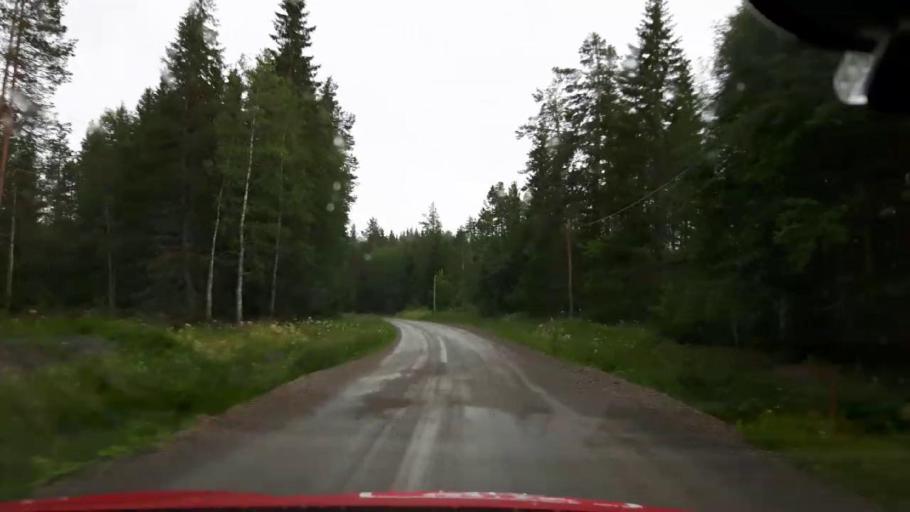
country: SE
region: Jaemtland
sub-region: OEstersunds Kommun
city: Brunflo
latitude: 62.9036
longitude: 14.8590
